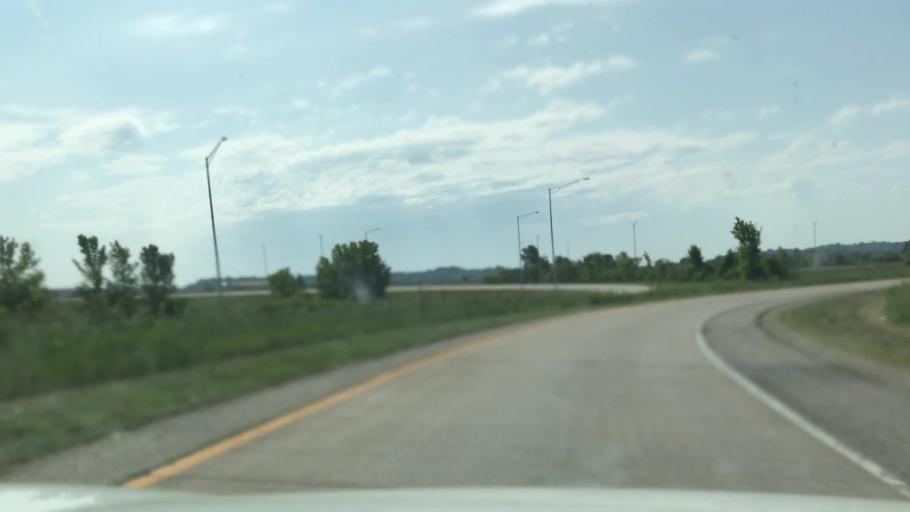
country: US
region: Illinois
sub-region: Saint Clair County
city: Washington Park
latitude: 38.6181
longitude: -90.0726
